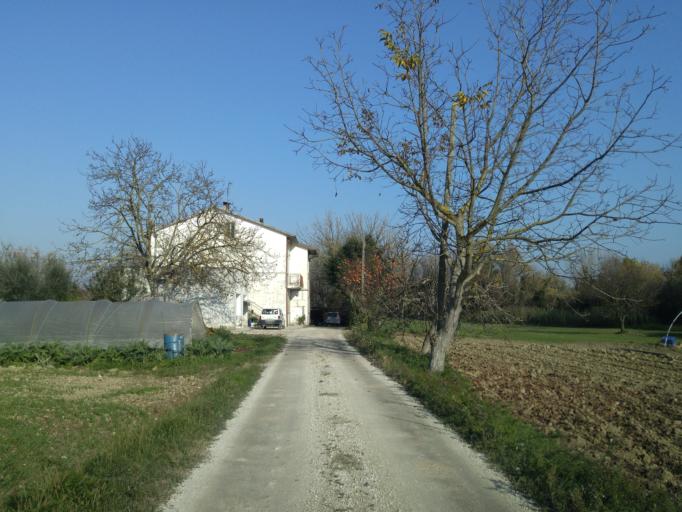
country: IT
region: The Marches
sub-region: Provincia di Pesaro e Urbino
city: Calcinelli
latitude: 43.7498
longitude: 12.9292
